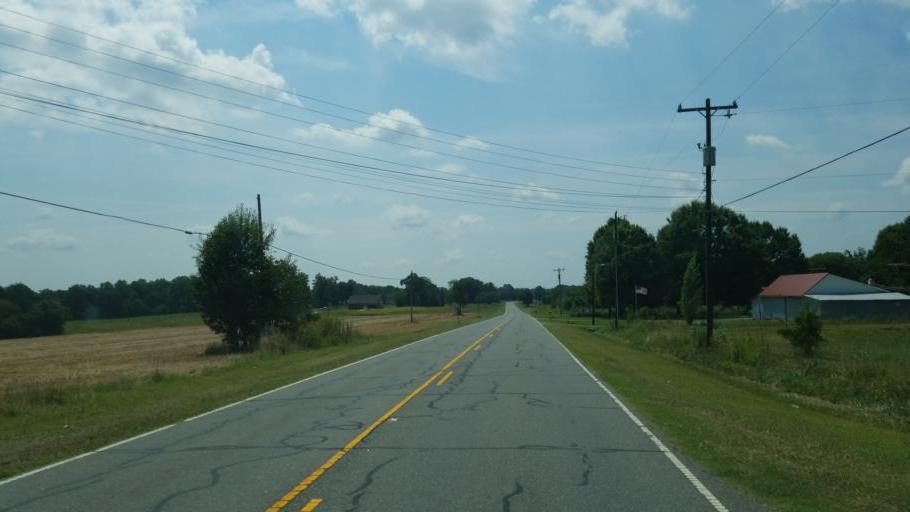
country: US
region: North Carolina
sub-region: Gaston County
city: Cherryville
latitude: 35.4357
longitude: -81.4193
